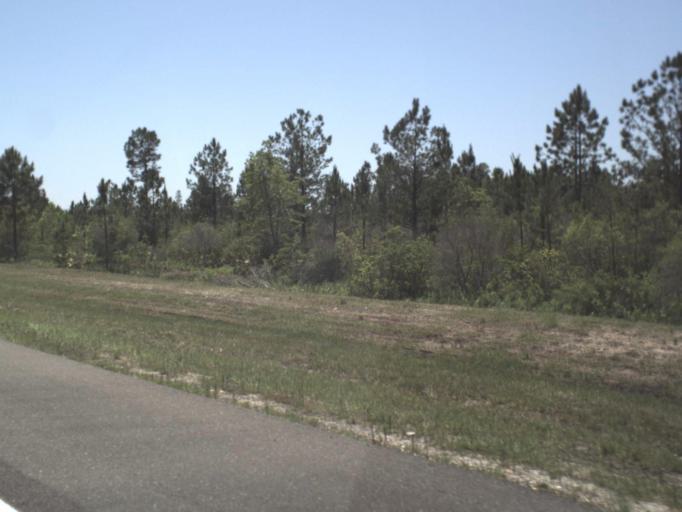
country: US
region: Florida
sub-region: Duval County
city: Baldwin
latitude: 30.2807
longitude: -81.8781
